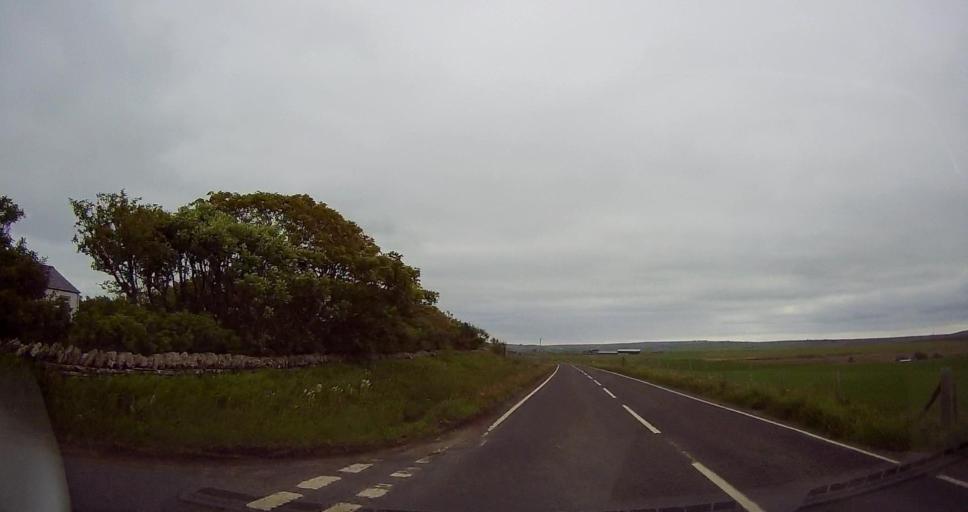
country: GB
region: Scotland
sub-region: Orkney Islands
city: Kirkwall
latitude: 58.9429
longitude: -2.8738
